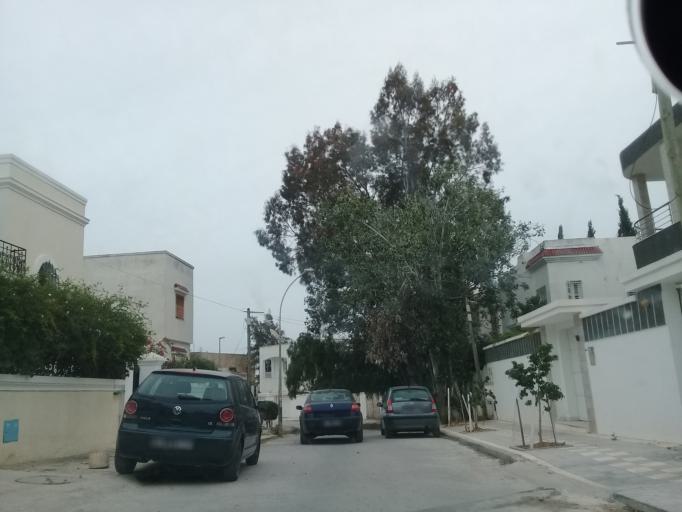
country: TN
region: Tunis
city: Tunis
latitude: 36.8431
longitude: 10.1516
